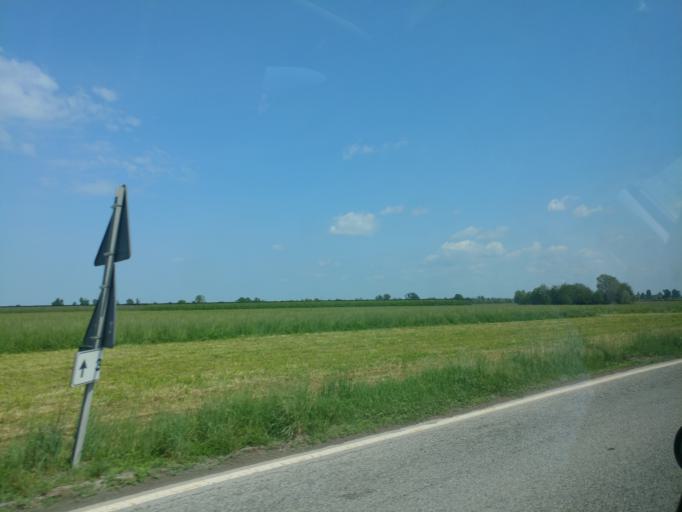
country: IT
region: Piedmont
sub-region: Provincia di Cuneo
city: Carde
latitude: 44.7328
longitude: 7.4240
